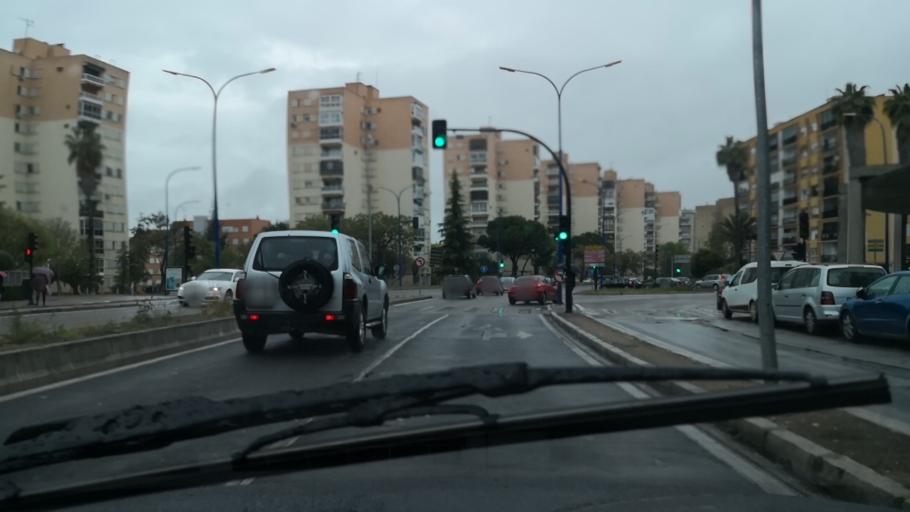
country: ES
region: Extremadura
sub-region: Provincia de Badajoz
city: Badajoz
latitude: 38.8726
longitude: -6.9805
